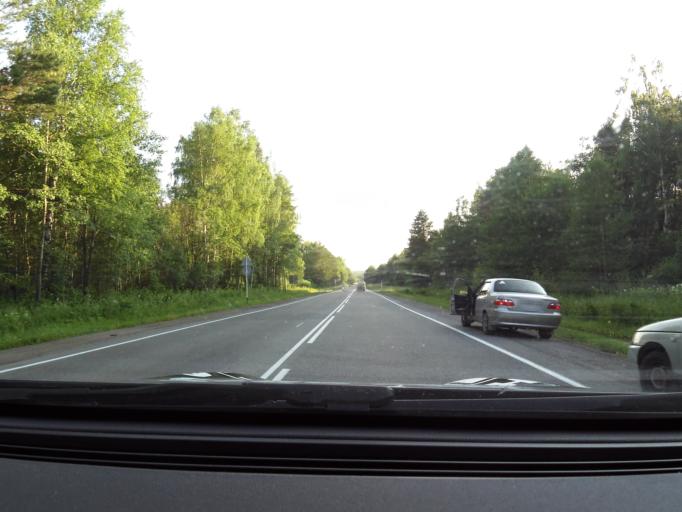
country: RU
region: Sverdlovsk
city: Atig
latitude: 56.7458
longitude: 59.4593
